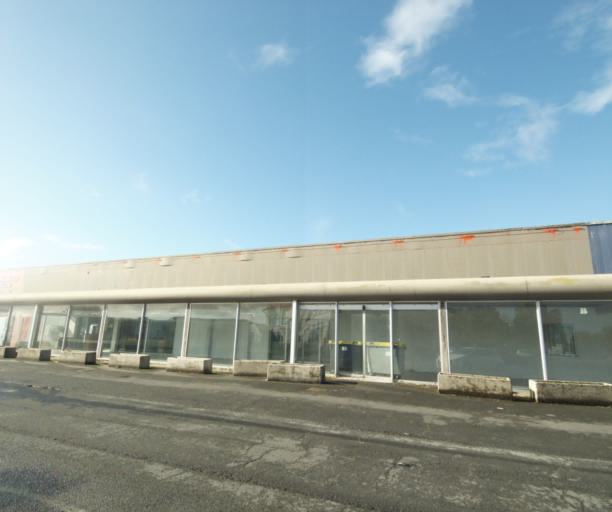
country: FR
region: Poitou-Charentes
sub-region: Departement de la Charente-Maritime
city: Breuil-Magne
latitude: 45.9514
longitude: -0.9364
